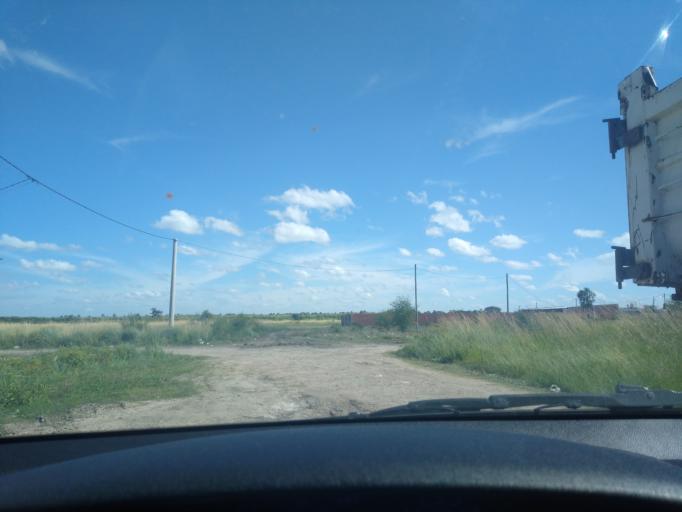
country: AR
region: Chaco
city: Resistencia
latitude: -27.4870
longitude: -59.0141
